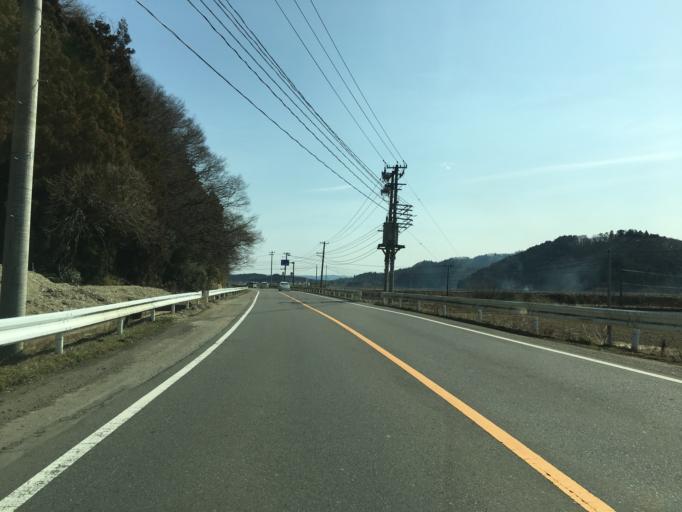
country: JP
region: Fukushima
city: Ishikawa
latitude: 37.1284
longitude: 140.3013
